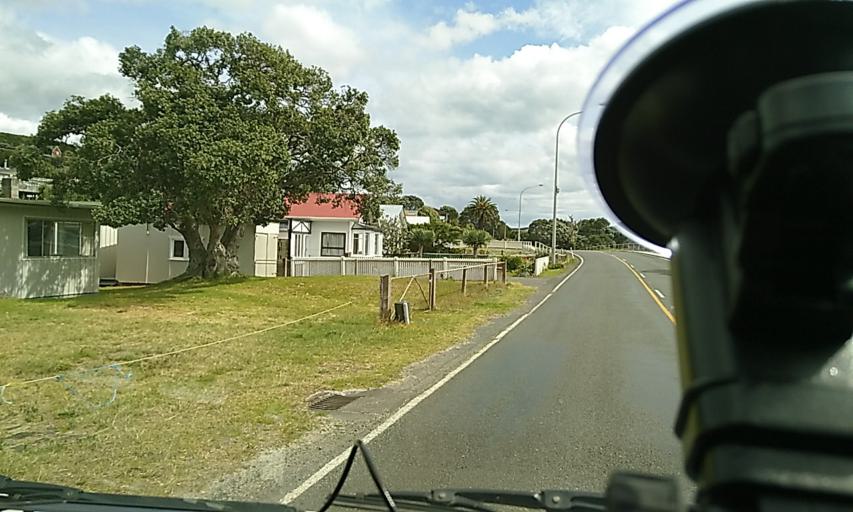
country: NZ
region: Northland
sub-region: Far North District
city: Ahipara
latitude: -35.5106
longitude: 173.3895
